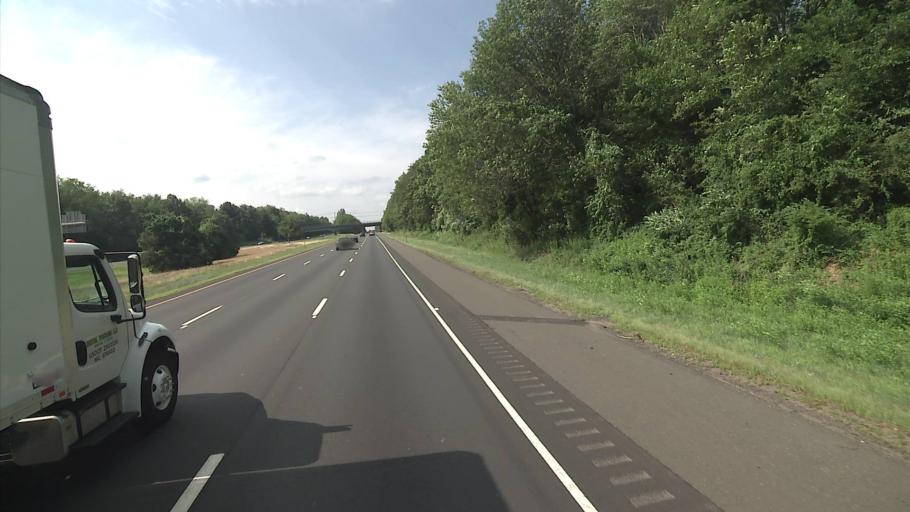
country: US
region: Connecticut
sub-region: New Haven County
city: Wallingford Center
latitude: 41.4699
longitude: -72.7743
